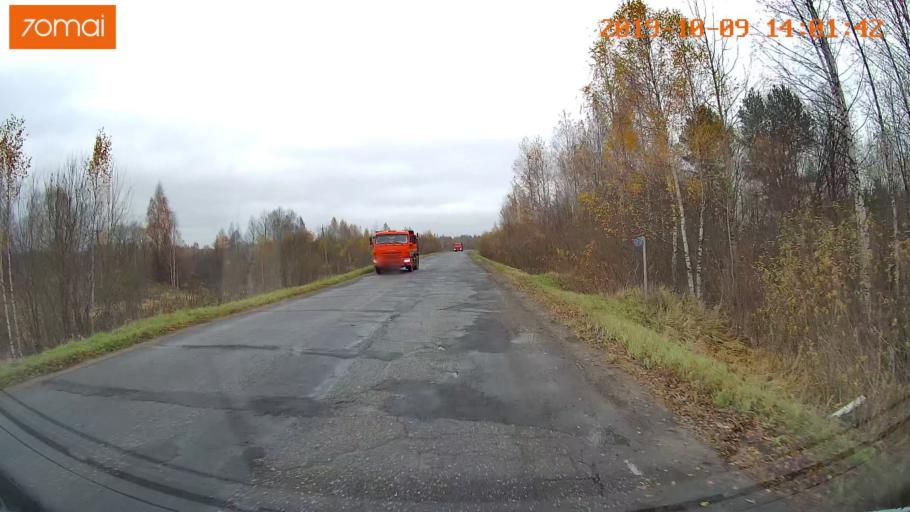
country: RU
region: Kostroma
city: Buy
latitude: 58.4451
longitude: 41.3496
